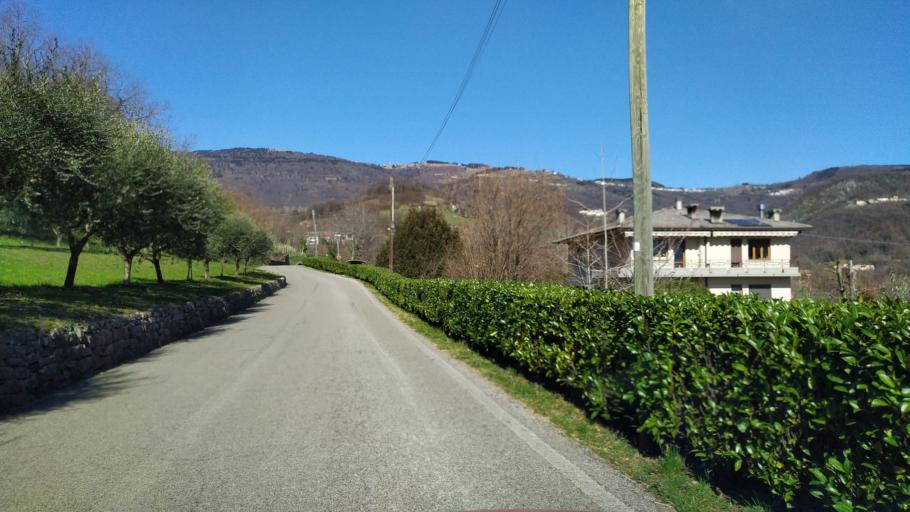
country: IT
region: Veneto
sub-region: Provincia di Vicenza
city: Fara Vicentino
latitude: 45.7571
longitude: 11.5421
